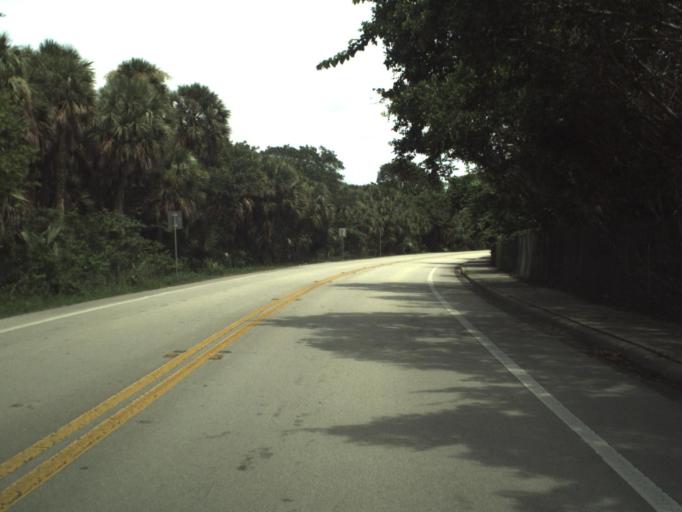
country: US
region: Florida
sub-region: Palm Beach County
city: North Palm Beach
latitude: 26.8325
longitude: -80.0483
